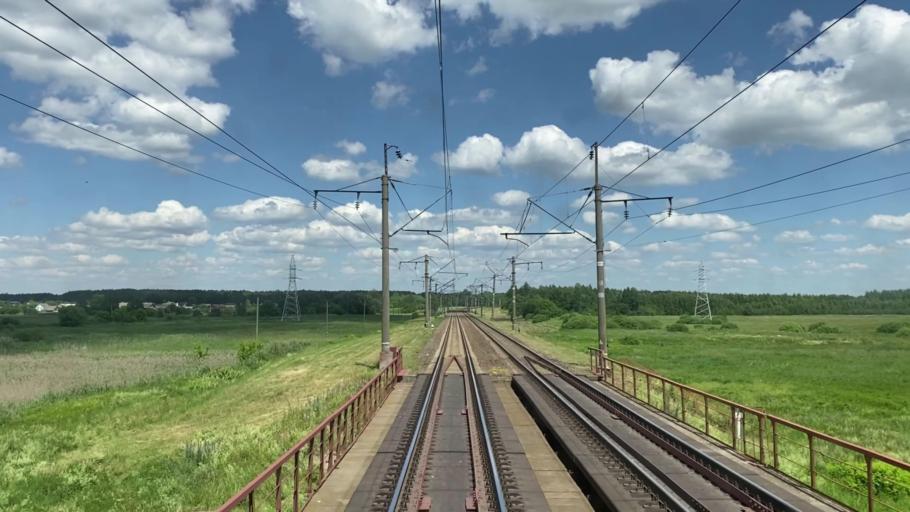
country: BY
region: Brest
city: Ivatsevichy
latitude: 52.7209
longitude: 25.3580
